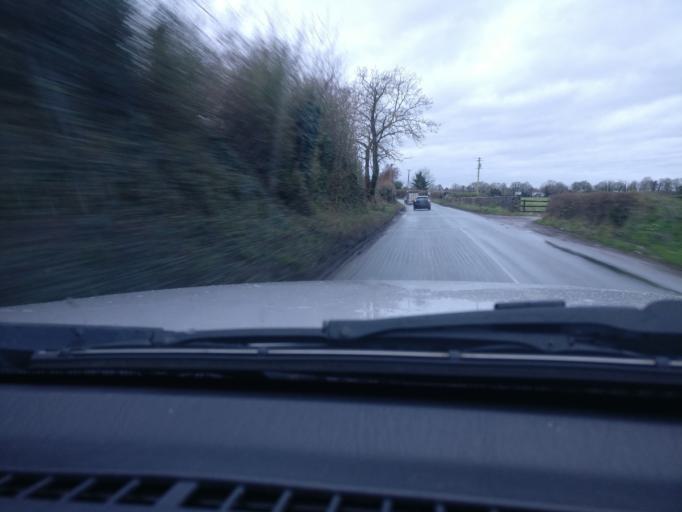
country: IE
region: Leinster
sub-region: An Mhi
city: Longwood
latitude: 53.4512
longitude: -6.9587
